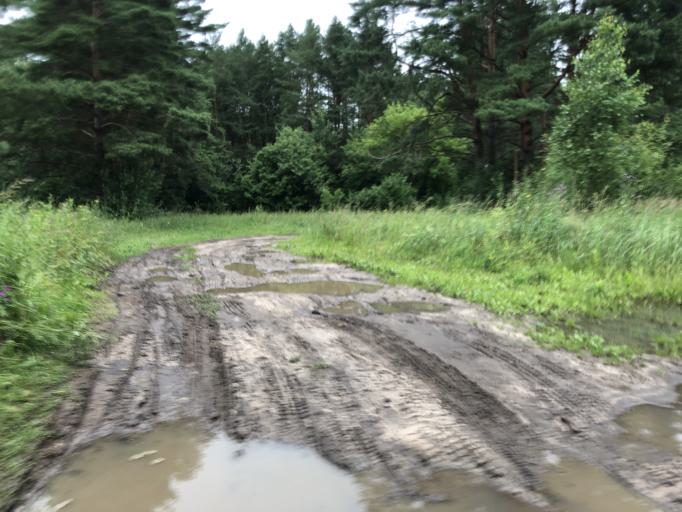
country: RU
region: Tverskaya
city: Rzhev
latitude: 56.2463
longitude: 34.3705
